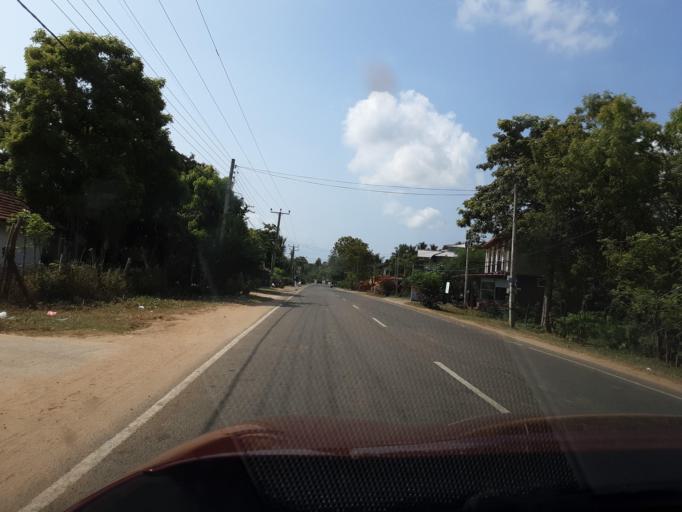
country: LK
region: Southern
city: Tangalla
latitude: 6.3009
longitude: 81.2357
